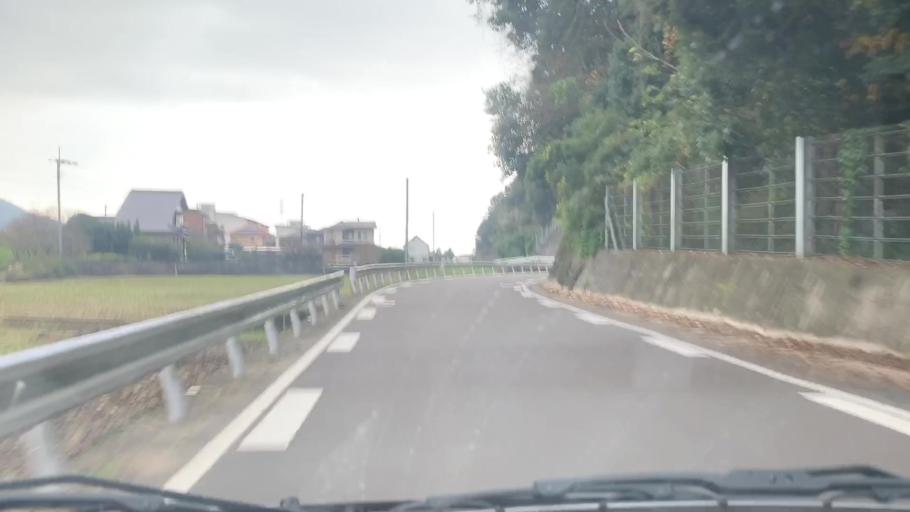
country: JP
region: Saga Prefecture
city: Kashima
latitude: 33.1235
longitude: 130.0534
